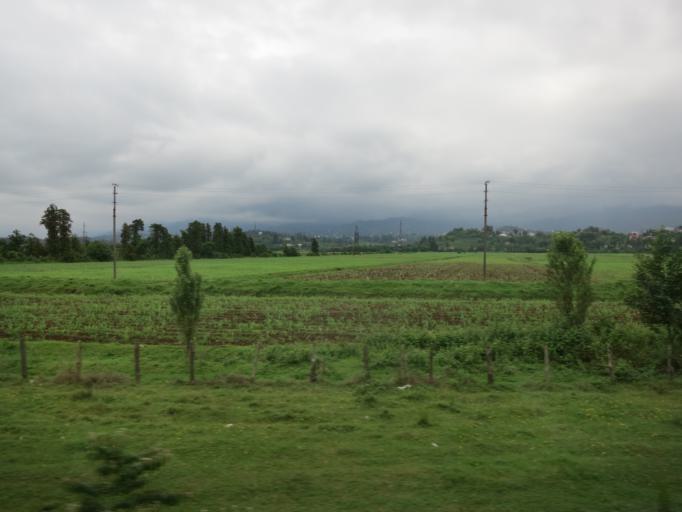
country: GE
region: Ajaria
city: Kobuleti
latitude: 41.7929
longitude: 41.7699
